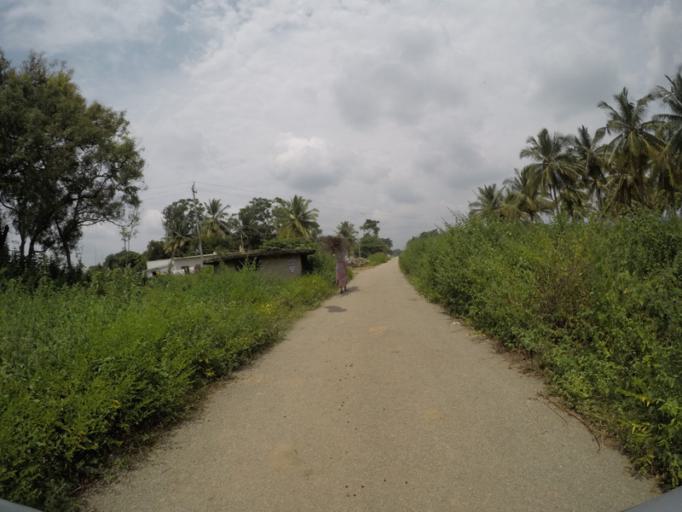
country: IN
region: Karnataka
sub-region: Ramanagara
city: Kanakapura
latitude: 12.5661
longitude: 77.4219
